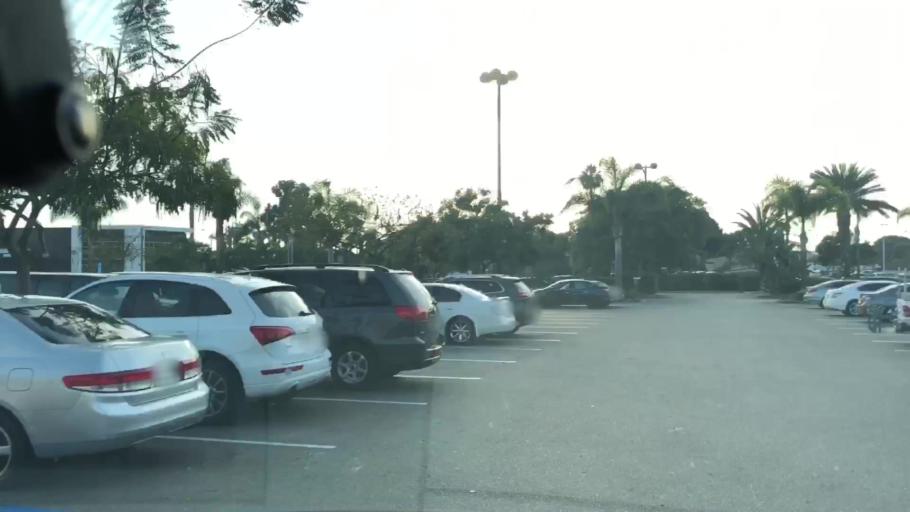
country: US
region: California
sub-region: Ventura County
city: Ventura
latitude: 34.2662
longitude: -119.2451
